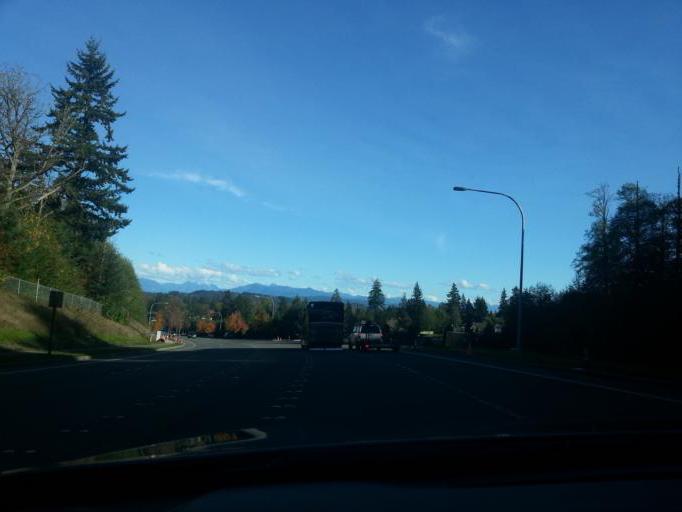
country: US
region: Washington
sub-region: Snohomish County
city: Silver Firs
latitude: 47.8632
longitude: -122.1331
